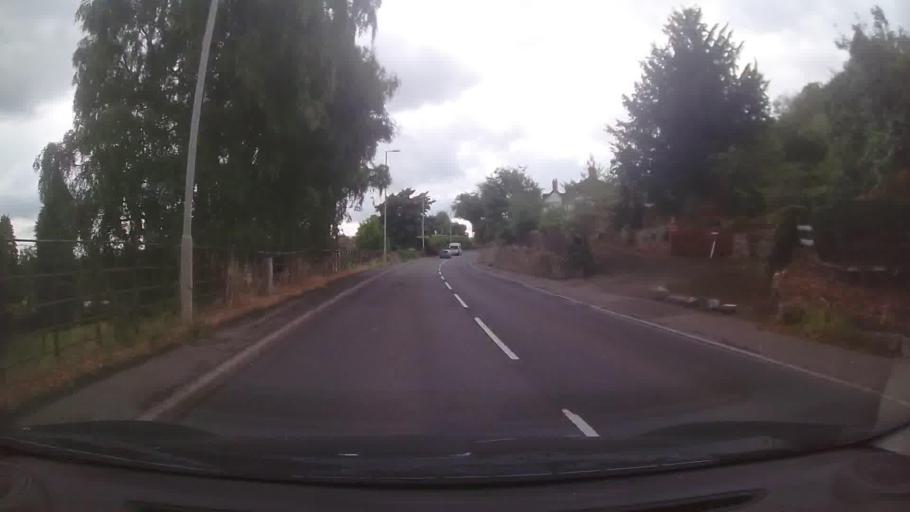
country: GB
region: England
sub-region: Shropshire
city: Pant
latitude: 52.7933
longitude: -3.0765
